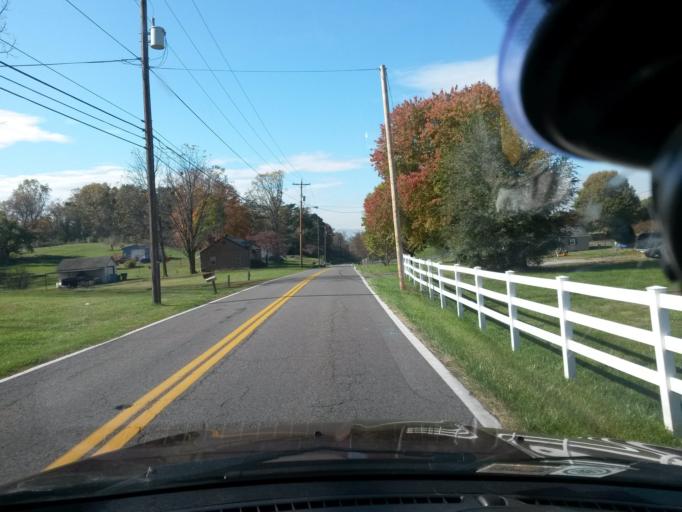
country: US
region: Virginia
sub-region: Roanoke County
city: Vinton
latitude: 37.2992
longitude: -79.9123
